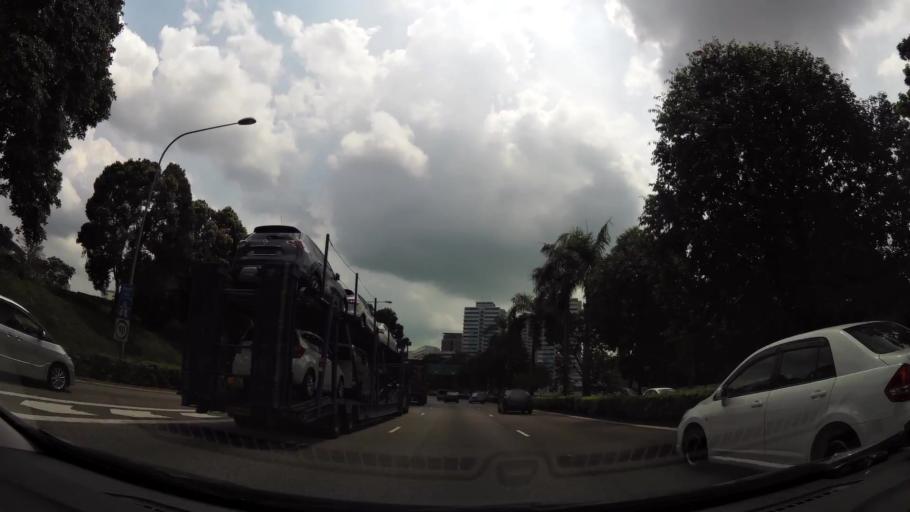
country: SG
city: Singapore
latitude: 1.3077
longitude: 103.7666
